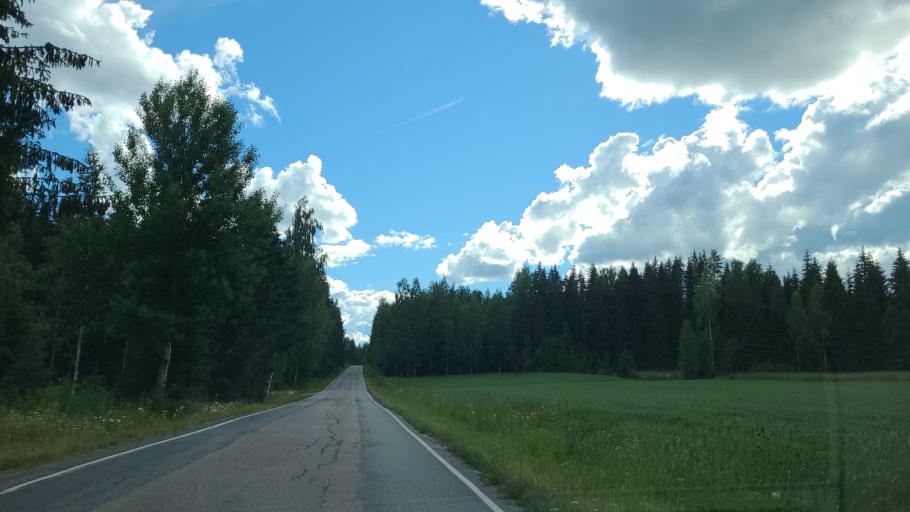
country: FI
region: Central Finland
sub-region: Jaemsae
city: Jaemsae
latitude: 61.8923
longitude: 25.2558
